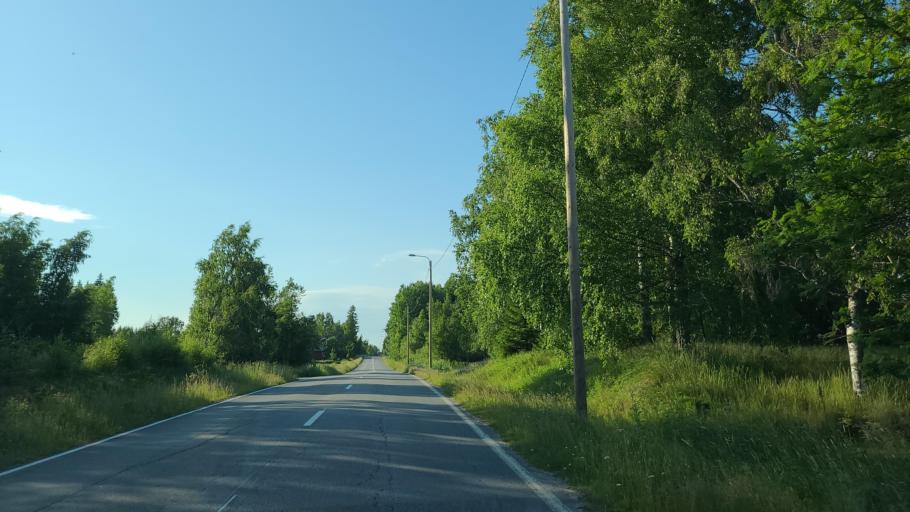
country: FI
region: Ostrobothnia
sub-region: Vaasa
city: Replot
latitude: 63.3281
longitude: 21.3402
